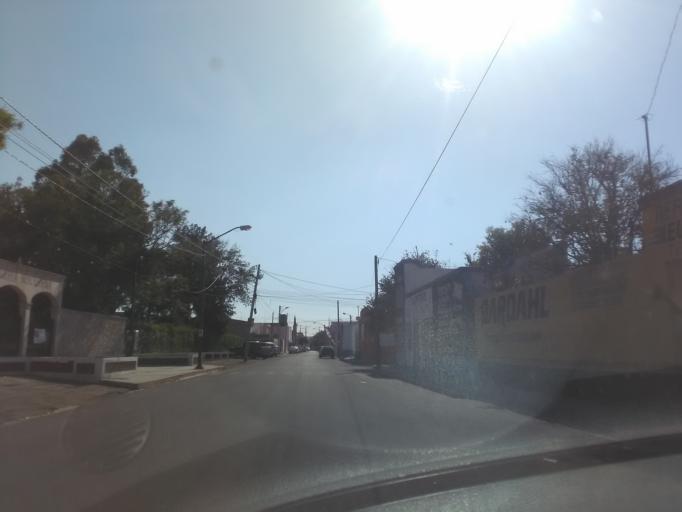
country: MX
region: Durango
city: Victoria de Durango
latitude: 24.0309
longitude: -104.6622
